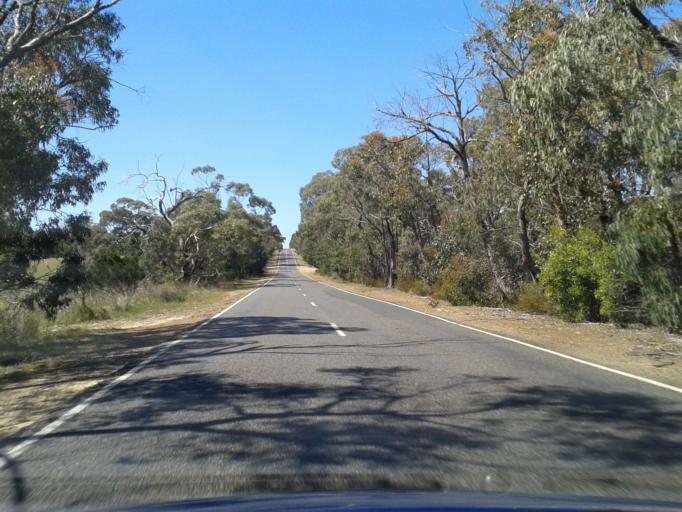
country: AU
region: Victoria
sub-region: Northern Grampians
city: Stawell
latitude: -37.1545
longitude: 142.5761
